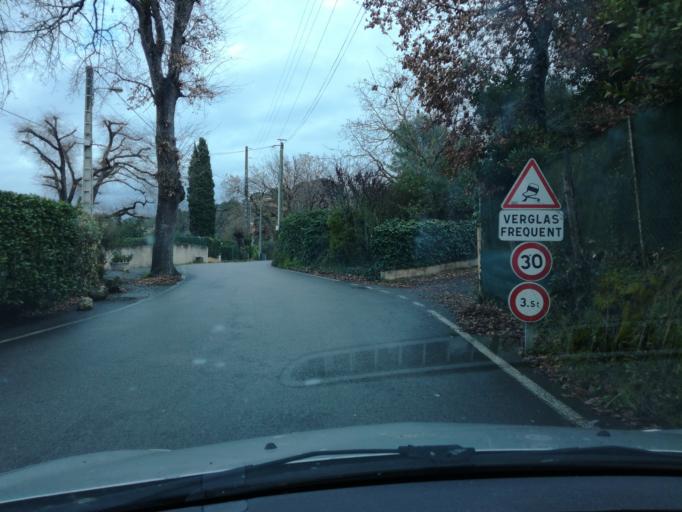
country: FR
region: Provence-Alpes-Cote d'Azur
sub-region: Departement des Alpes-Maritimes
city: Mouans-Sartoux
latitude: 43.6056
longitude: 6.9781
